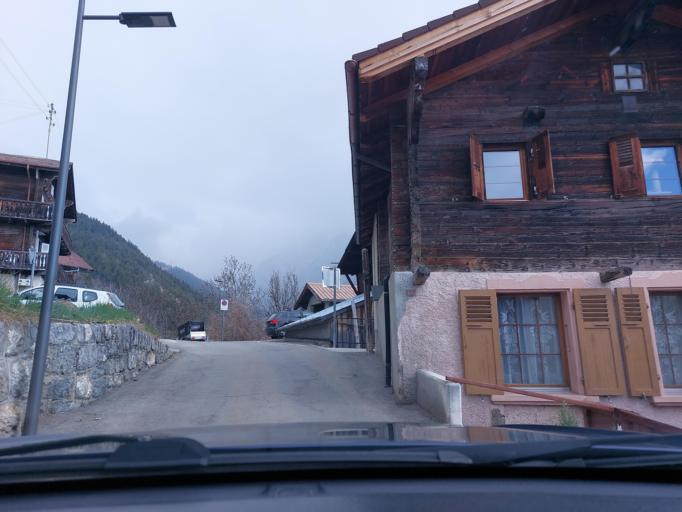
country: CH
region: Valais
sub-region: Conthey District
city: Conthey
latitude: 46.2593
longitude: 7.3102
